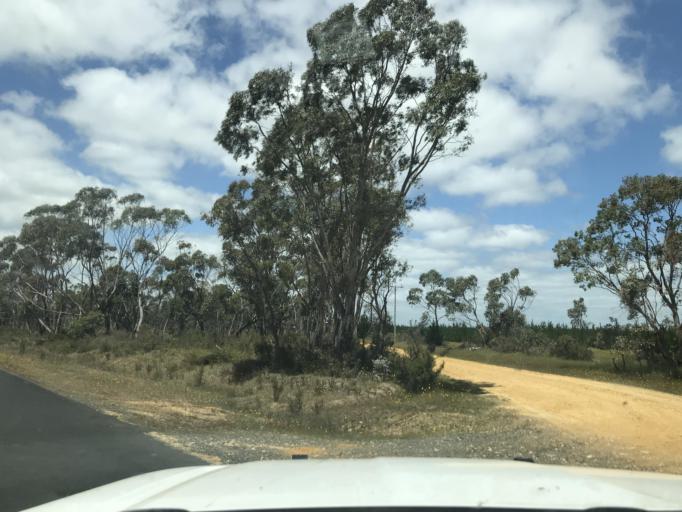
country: AU
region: South Australia
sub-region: Wattle Range
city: Penola
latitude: -37.3620
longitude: 141.1505
